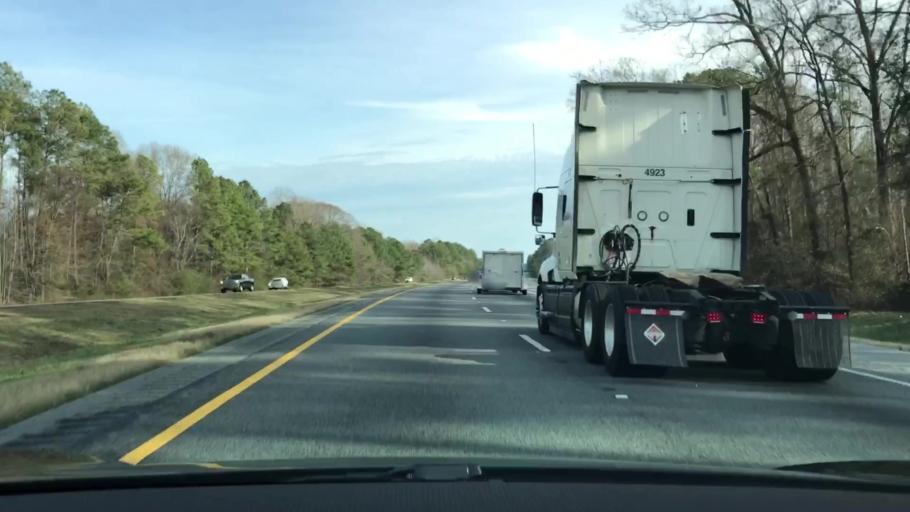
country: US
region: Georgia
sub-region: Morgan County
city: Madison
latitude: 33.5771
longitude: -83.5339
